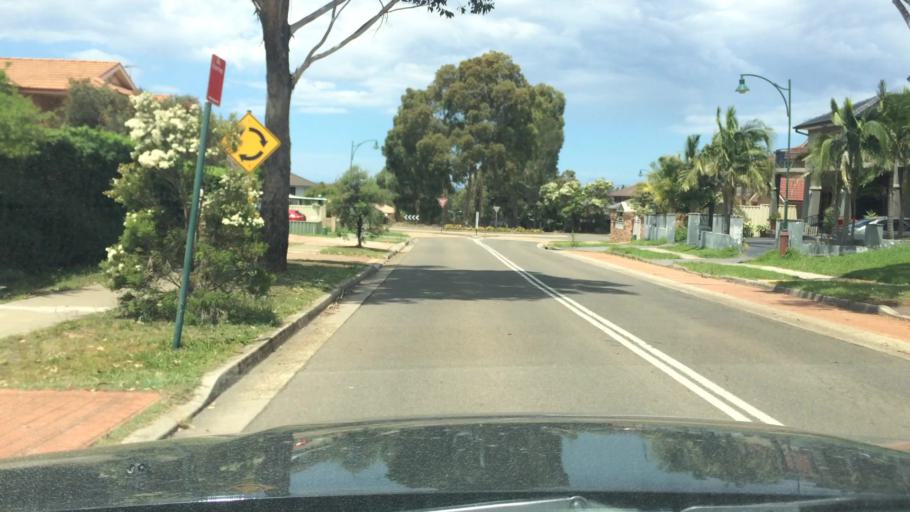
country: AU
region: New South Wales
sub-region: Campbelltown Municipality
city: Denham Court
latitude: -33.9419
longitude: 150.8343
